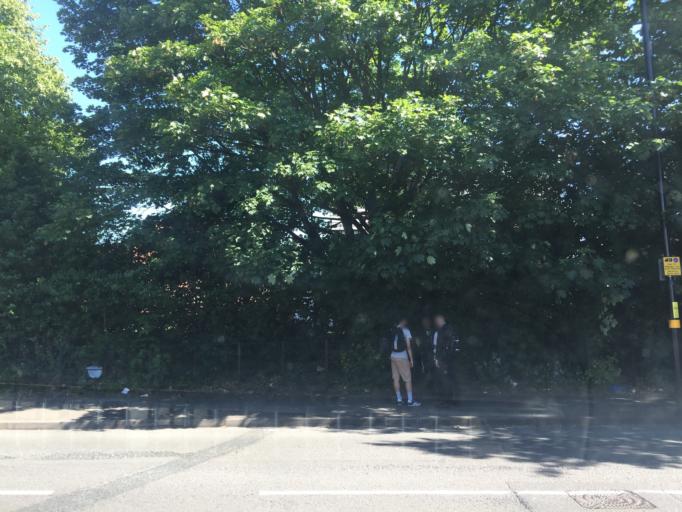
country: GB
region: England
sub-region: Sandwell
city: Smethwick
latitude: 52.4818
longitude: -1.9490
